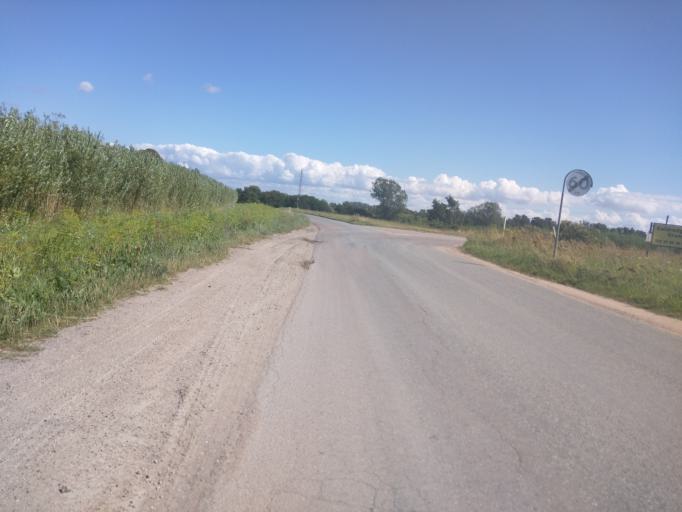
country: DK
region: Zealand
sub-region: Kalundborg Kommune
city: Svebolle
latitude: 55.6899
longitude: 11.2863
